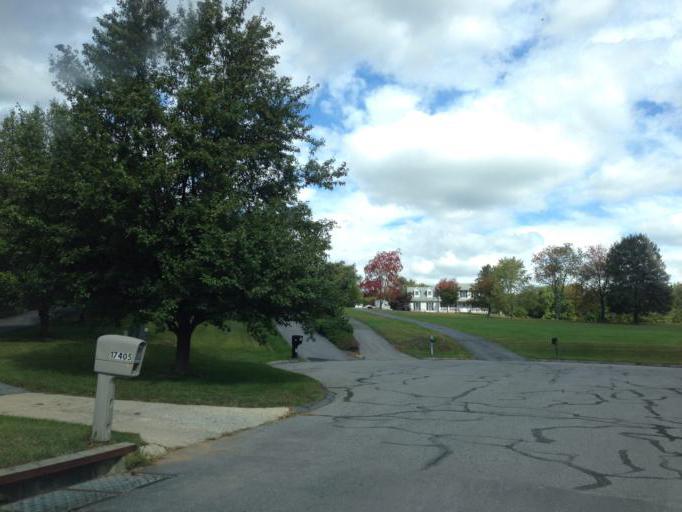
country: US
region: Maryland
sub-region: Carroll County
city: Mount Airy
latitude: 39.3505
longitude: -77.1200
